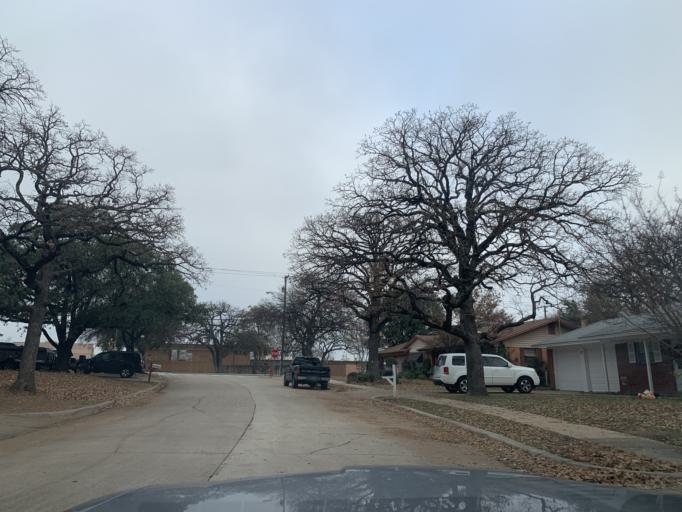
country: US
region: Texas
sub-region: Tarrant County
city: Bedford
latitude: 32.8352
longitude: -97.1571
